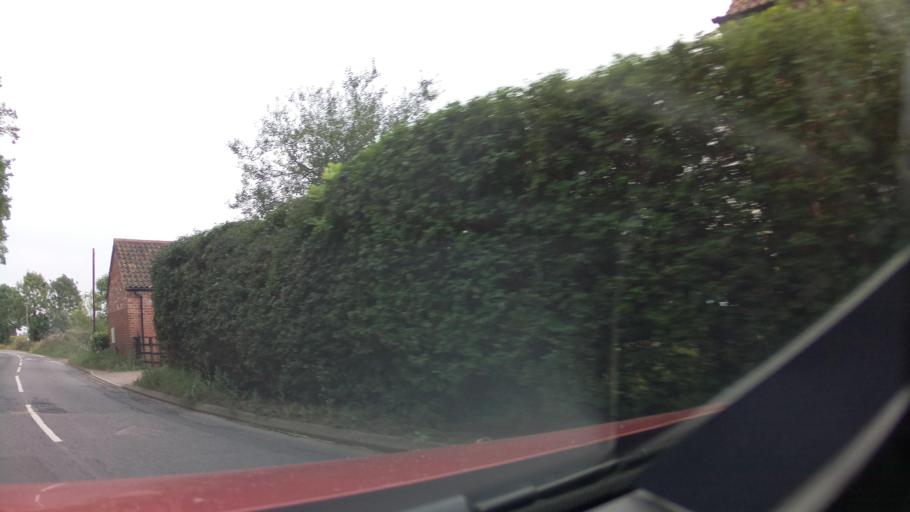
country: GB
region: England
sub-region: Lincolnshire
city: Skellingthorpe
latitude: 53.1424
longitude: -0.6458
